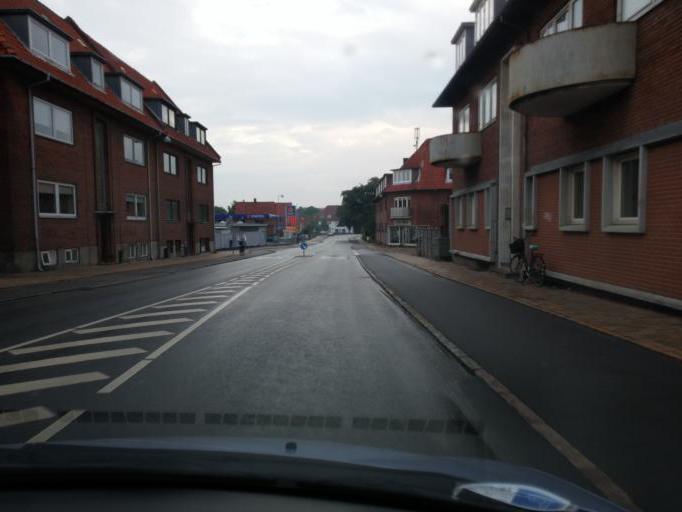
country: DK
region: South Denmark
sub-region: Odense Kommune
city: Odense
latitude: 55.4068
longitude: 10.4034
